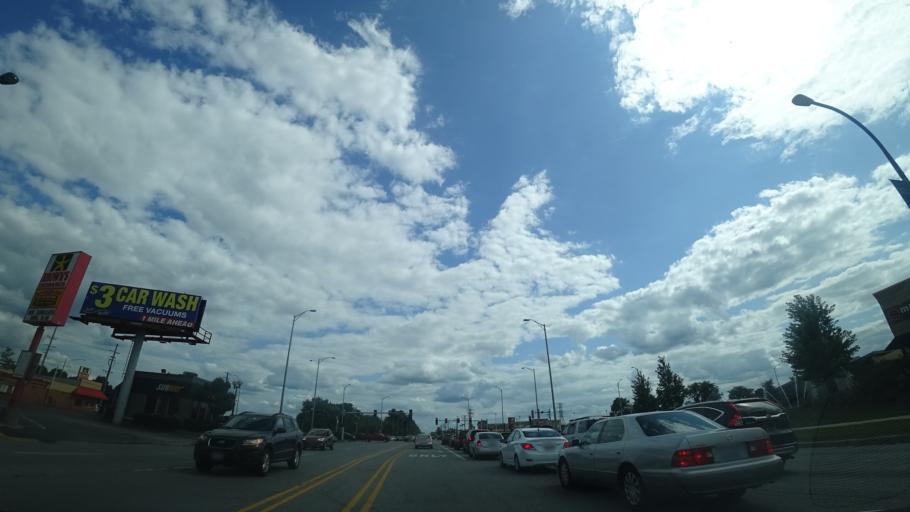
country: US
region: Illinois
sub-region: Cook County
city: Alsip
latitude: 41.6918
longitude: -87.7398
